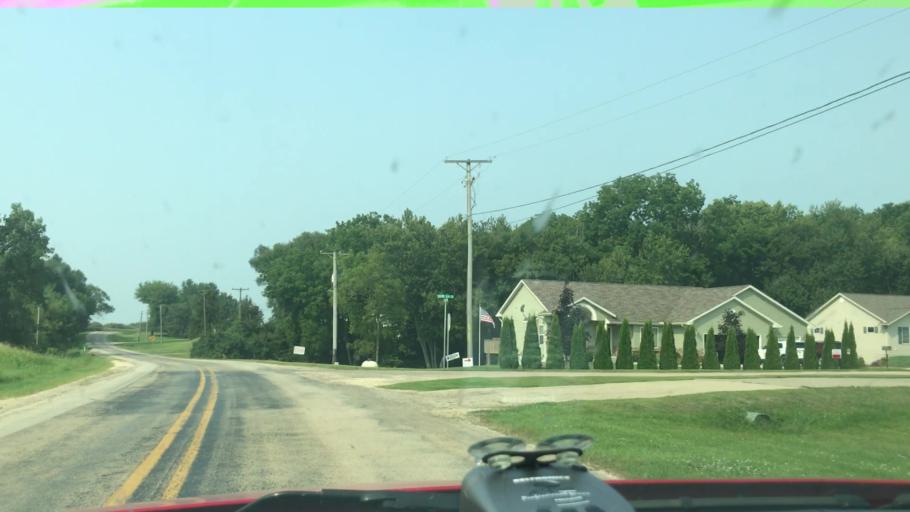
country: US
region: Illinois
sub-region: Whiteside County
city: Erie
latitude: 41.7069
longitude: -90.0884
